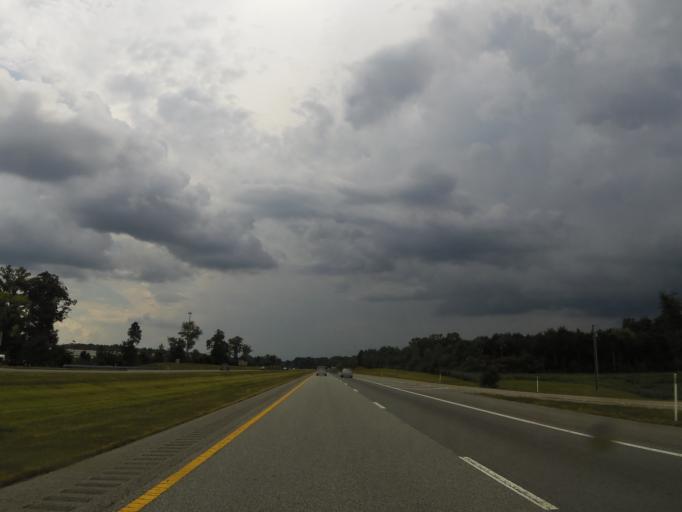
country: US
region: Tennessee
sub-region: Wilson County
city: Rural Hill
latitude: 36.0661
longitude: -86.4310
